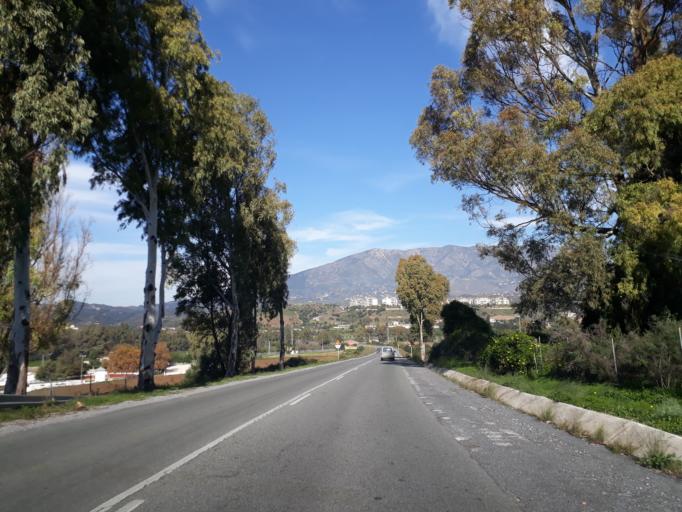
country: ES
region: Andalusia
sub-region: Provincia de Malaga
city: Fuengirola
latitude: 36.5388
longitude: -4.6877
